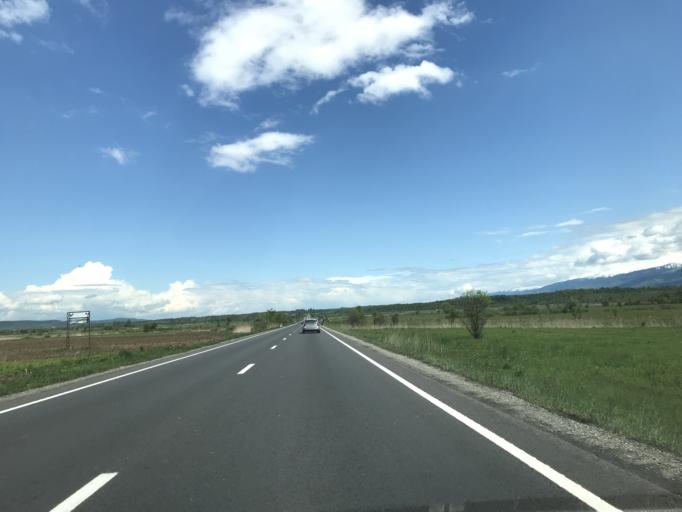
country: RO
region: Sibiu
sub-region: Comuna Porumbacu de Jos
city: Porumbacu de Jos
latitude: 45.7569
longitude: 24.4745
